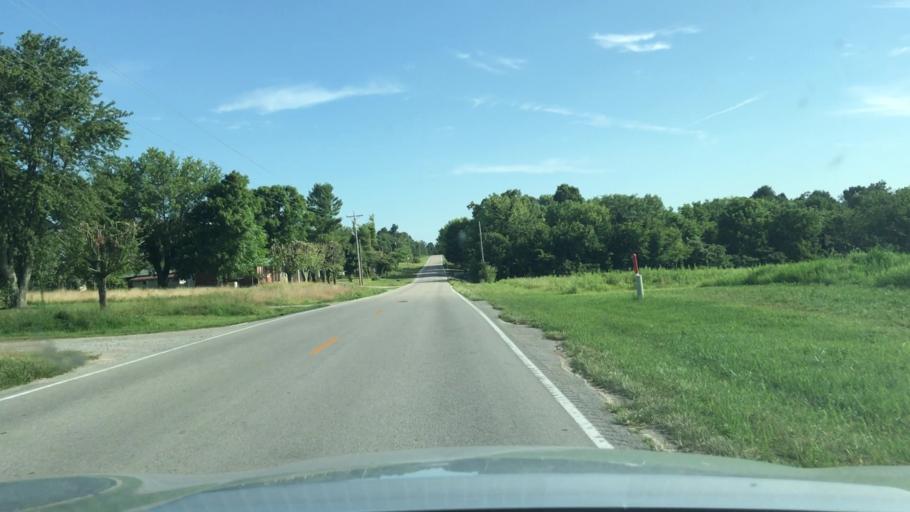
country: US
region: Kentucky
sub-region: Todd County
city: Elkton
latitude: 36.9240
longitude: -87.1625
